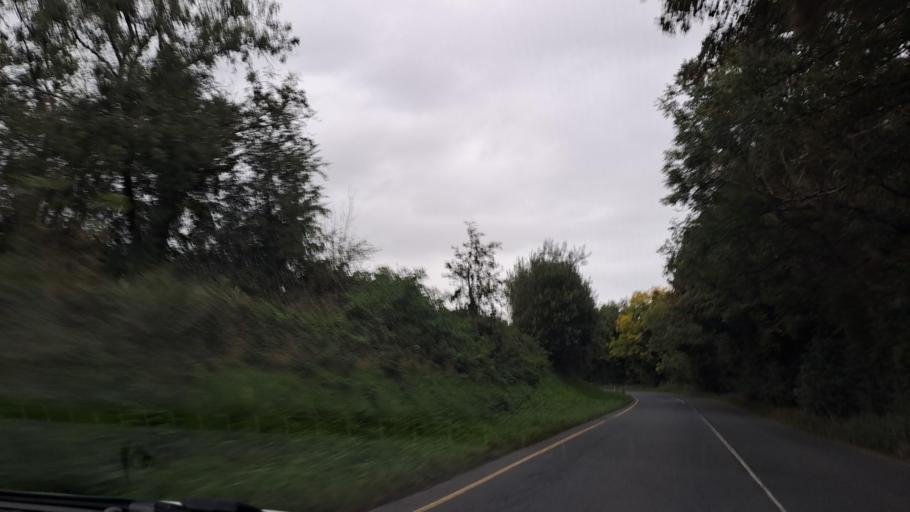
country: IE
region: Ulster
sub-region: County Monaghan
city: Monaghan
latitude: 54.2311
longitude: -6.9584
